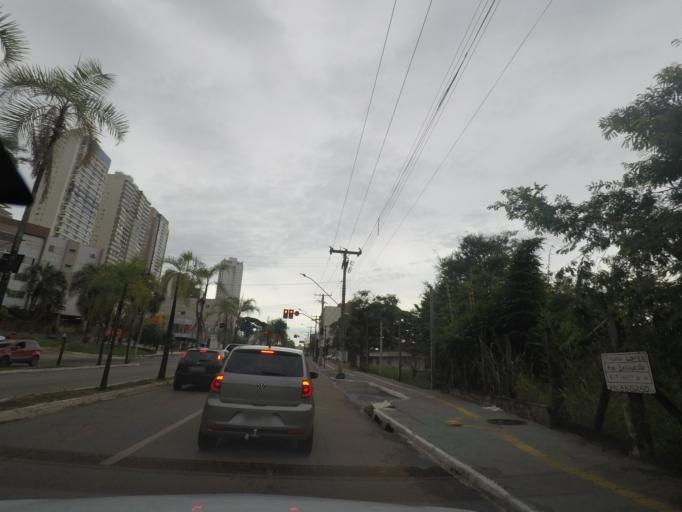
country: BR
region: Goias
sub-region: Goiania
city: Goiania
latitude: -16.7031
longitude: -49.2528
